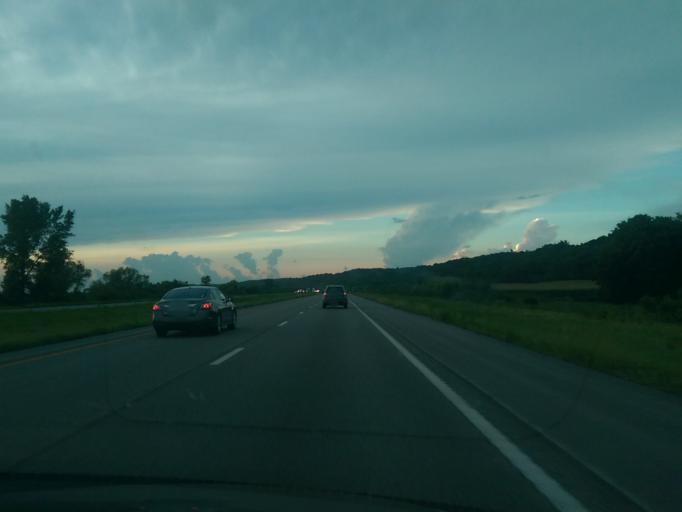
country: US
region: Missouri
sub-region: Atchison County
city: Rock Port
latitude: 40.3177
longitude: -95.4949
